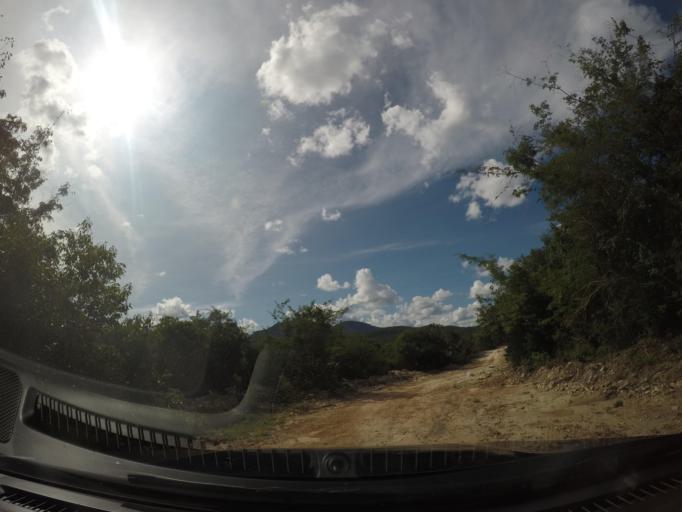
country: BR
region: Bahia
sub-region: Barra Da Estiva
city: Barra da Estiva
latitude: -13.1428
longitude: -41.5937
